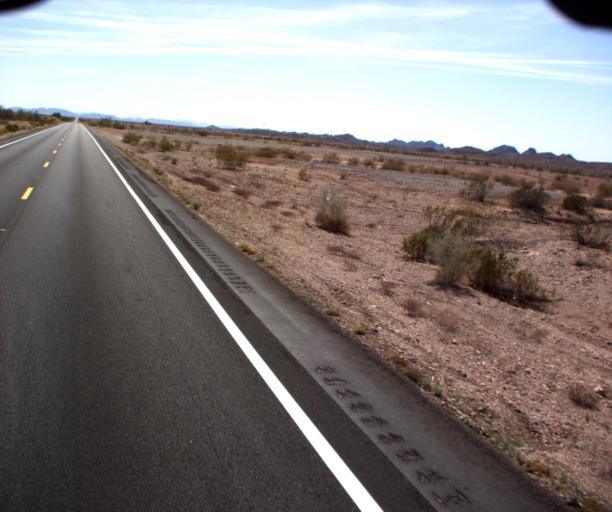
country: US
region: Arizona
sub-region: Yuma County
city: Wellton
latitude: 33.0571
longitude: -114.2922
